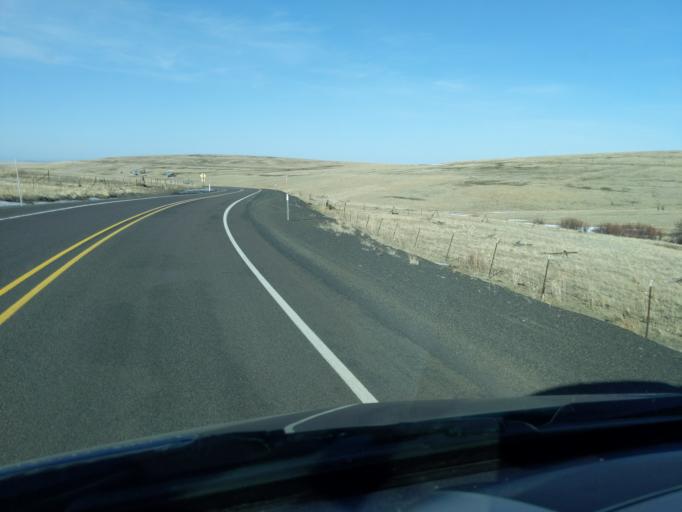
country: US
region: Oregon
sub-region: Umatilla County
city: Pilot Rock
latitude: 45.3085
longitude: -119.0022
